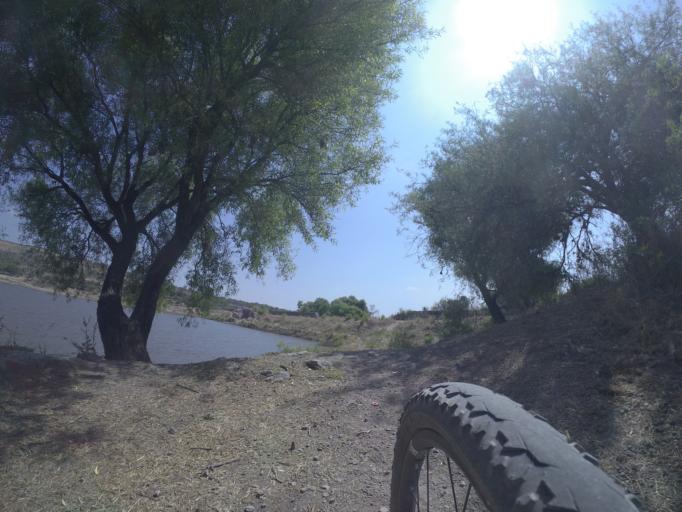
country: MX
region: Aguascalientes
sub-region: Jesus Maria
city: Paseos de las Haciendas [Fraccionamiento]
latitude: 21.9971
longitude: -102.3638
